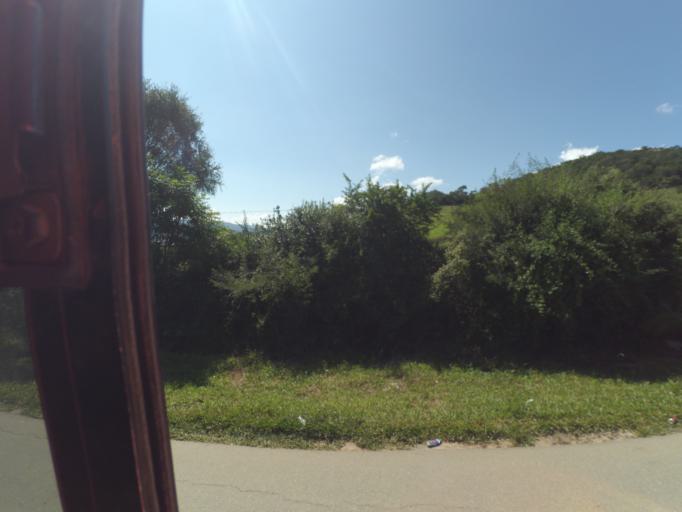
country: BO
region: Santa Cruz
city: Mairana
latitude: -18.1461
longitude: -63.9340
